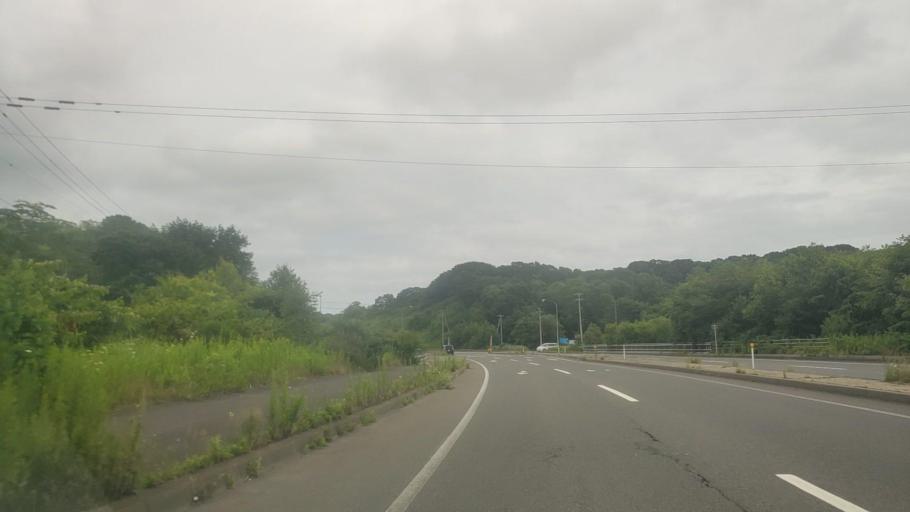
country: JP
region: Hokkaido
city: Shiraoi
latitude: 42.4563
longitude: 141.1892
